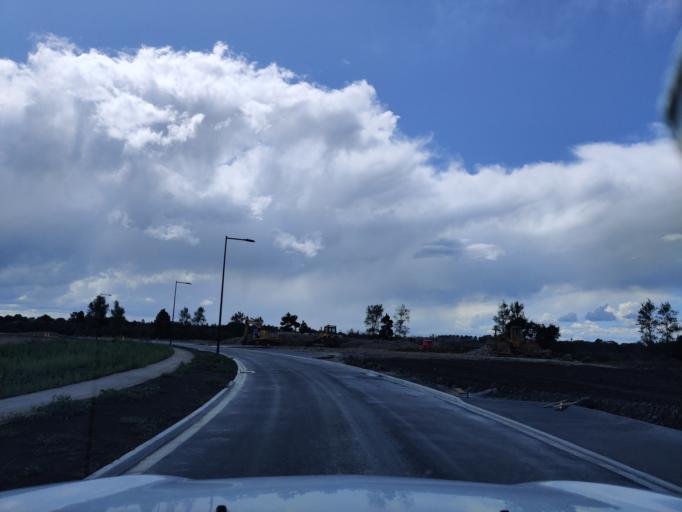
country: NZ
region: Waikato
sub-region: Waikato District
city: Te Kauwhata
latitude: -37.4113
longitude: 175.1530
